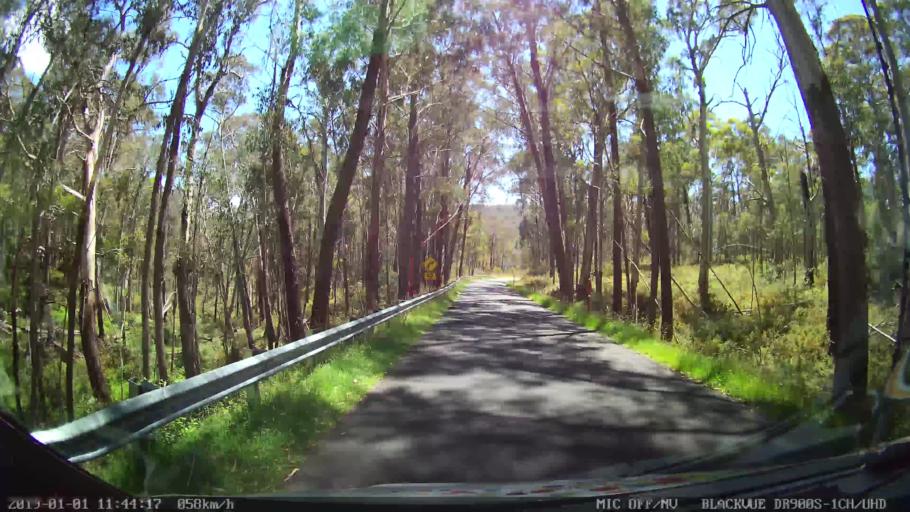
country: AU
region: New South Wales
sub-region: Snowy River
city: Jindabyne
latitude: -35.9011
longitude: 148.3914
